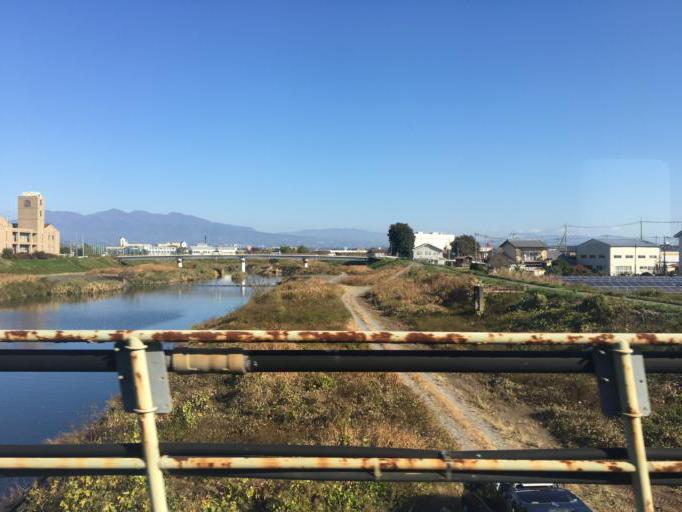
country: JP
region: Gunma
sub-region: Sawa-gun
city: Tamamura
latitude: 36.3528
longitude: 139.1428
